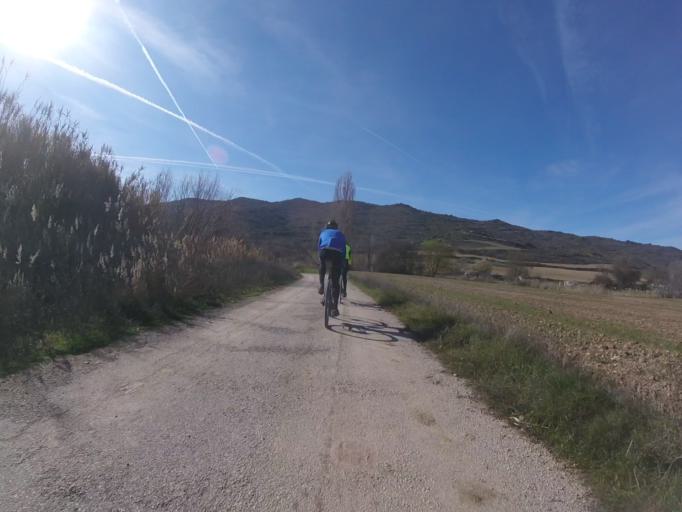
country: ES
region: Navarre
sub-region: Provincia de Navarra
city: Cirauqui
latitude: 42.6728
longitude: -1.9116
